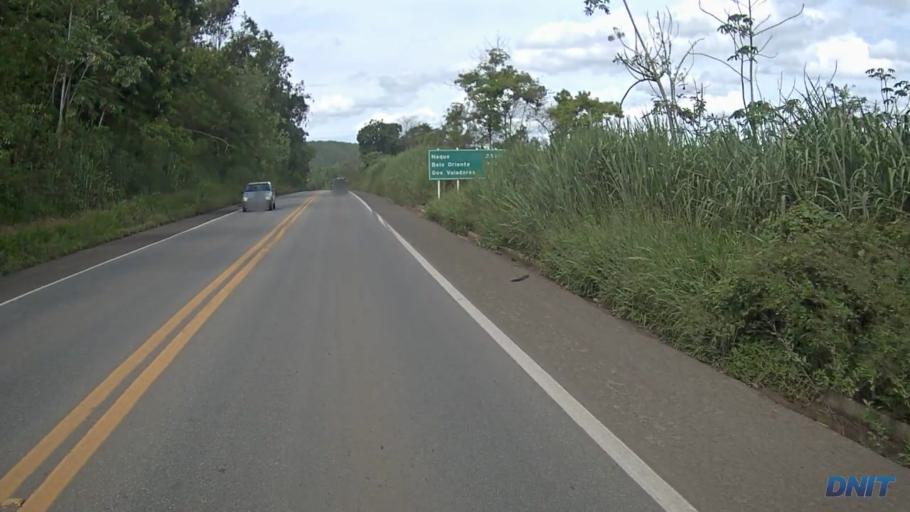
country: BR
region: Minas Gerais
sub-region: Ipaba
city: Ipaba
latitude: -19.3697
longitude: -42.4546
